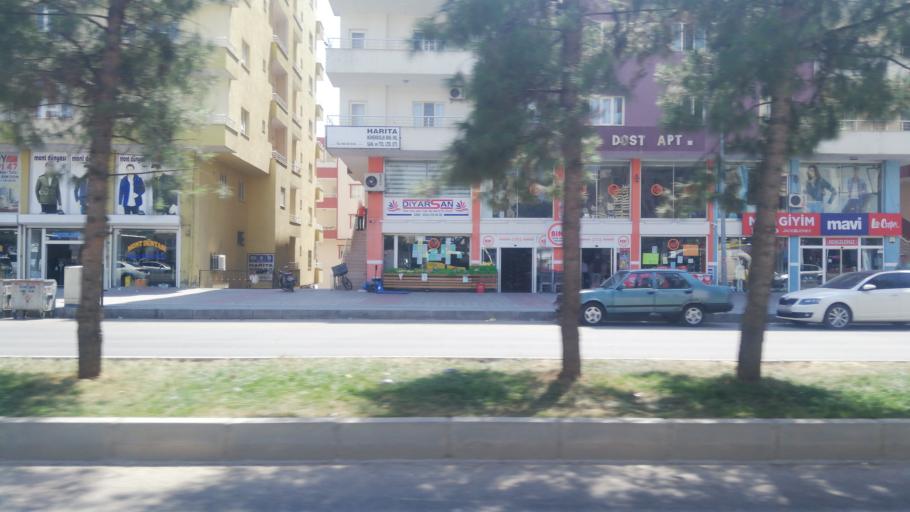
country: TR
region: Mardin
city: Midyat
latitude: 37.4165
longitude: 41.3654
